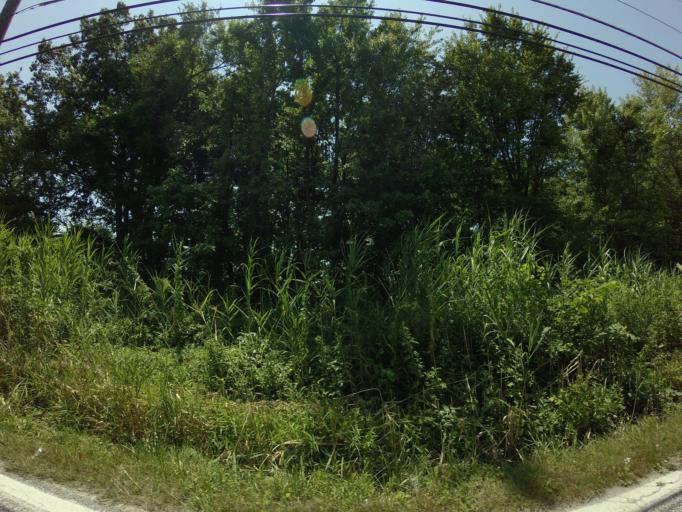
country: US
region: Maryland
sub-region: Baltimore County
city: Edgemere
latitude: 39.2713
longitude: -76.4678
